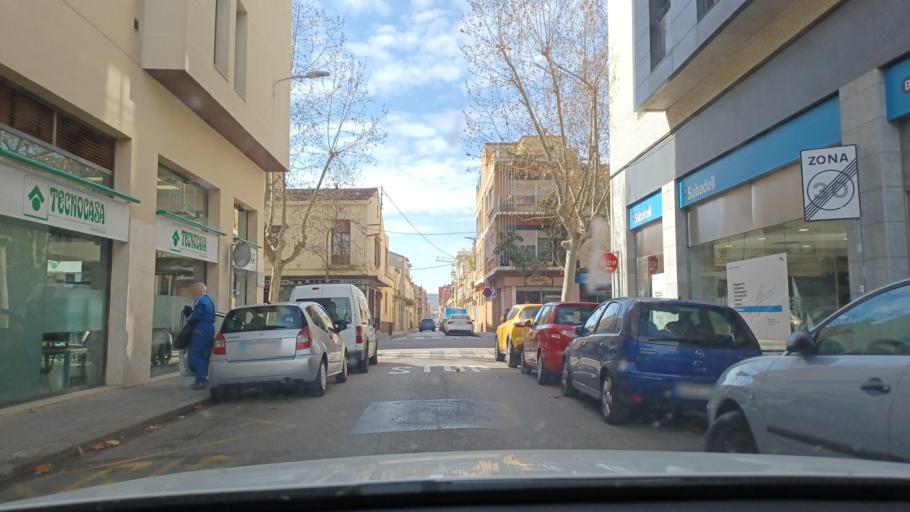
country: ES
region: Catalonia
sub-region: Provincia de Barcelona
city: Sabadell
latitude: 41.5386
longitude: 2.1134
